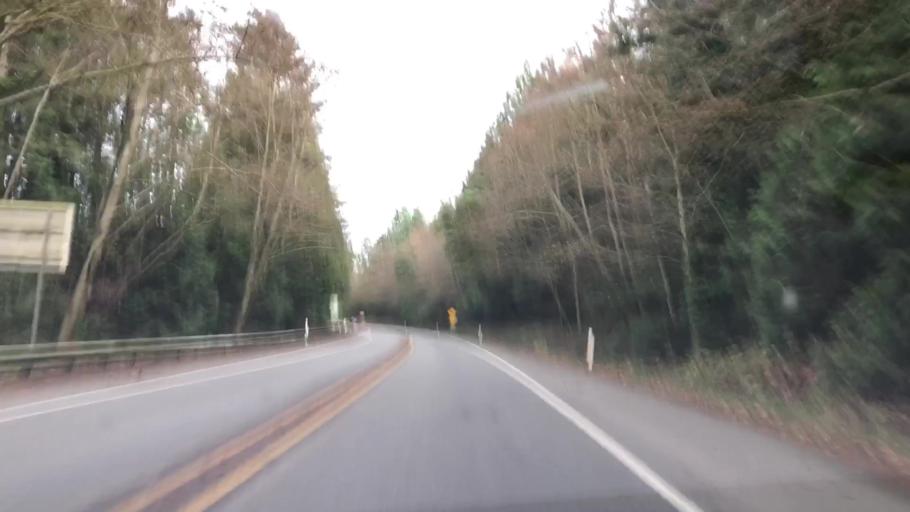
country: US
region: Washington
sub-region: Kitsap County
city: Bainbridge Island
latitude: 47.6385
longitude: -122.5153
